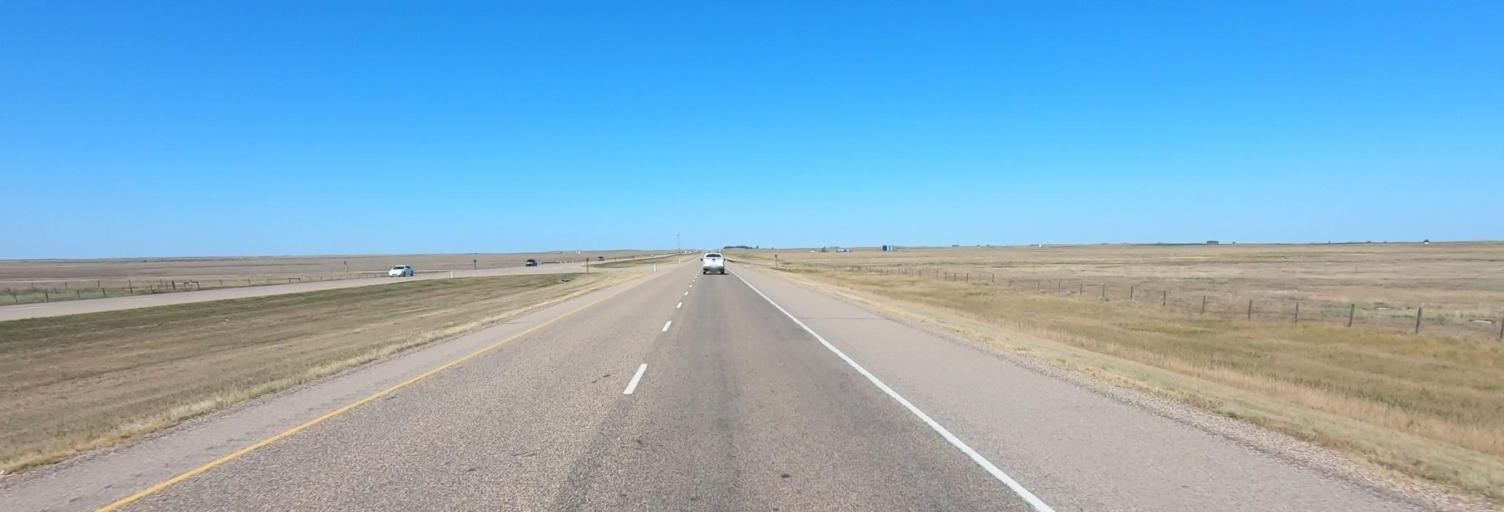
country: CA
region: Alberta
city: Brooks
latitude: 50.6682
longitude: -112.1262
